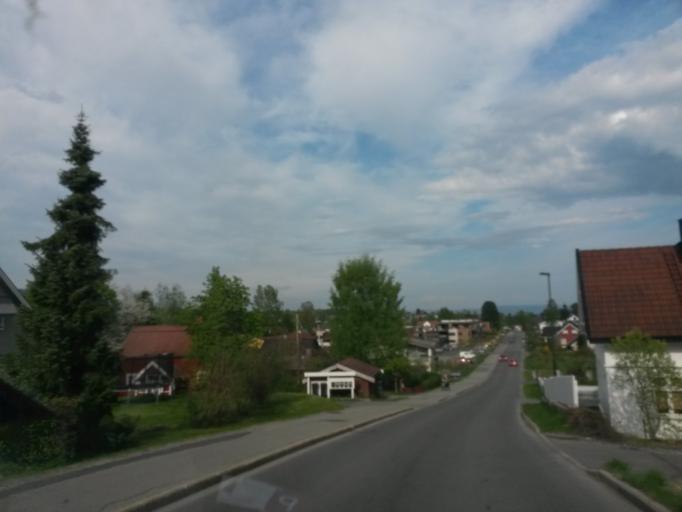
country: NO
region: Akershus
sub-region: Asker
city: Asker
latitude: 59.8344
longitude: 10.4140
